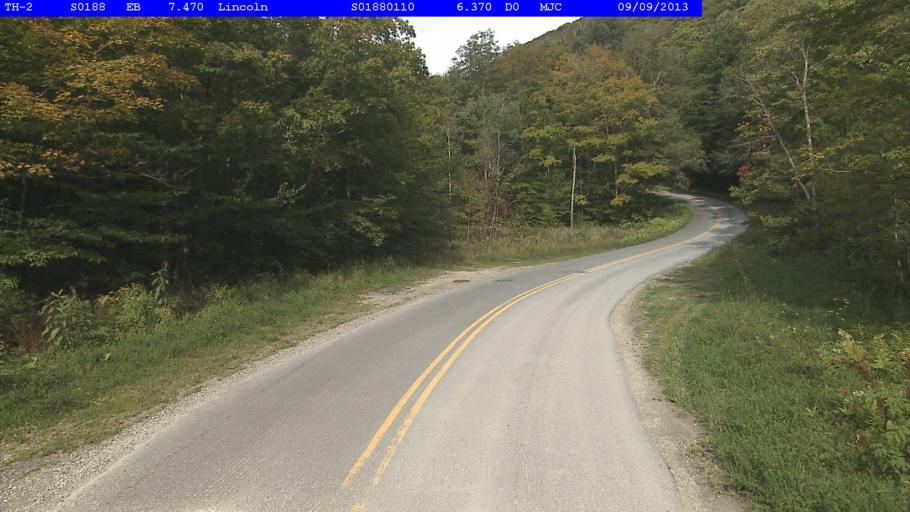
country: US
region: Vermont
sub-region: Addison County
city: Bristol
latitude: 44.0913
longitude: -72.9335
